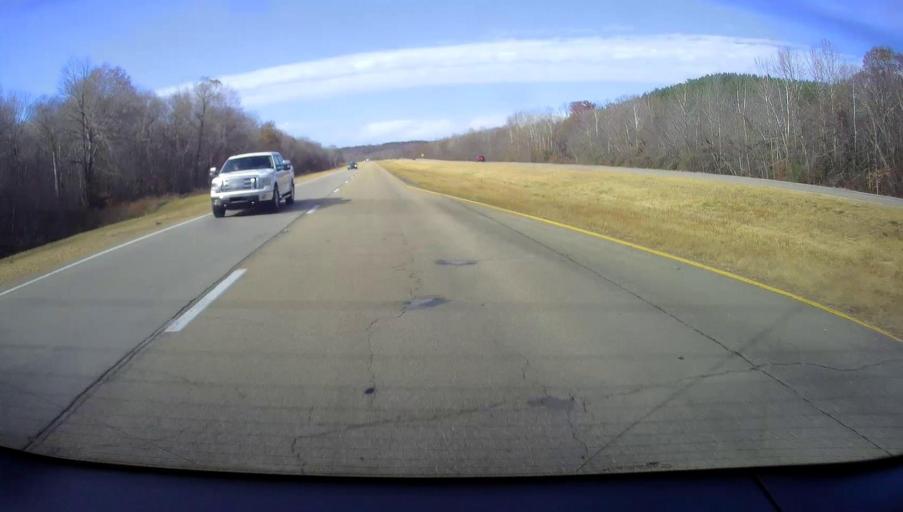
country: US
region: Mississippi
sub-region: Alcorn County
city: Corinth
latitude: 34.9398
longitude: -88.7798
